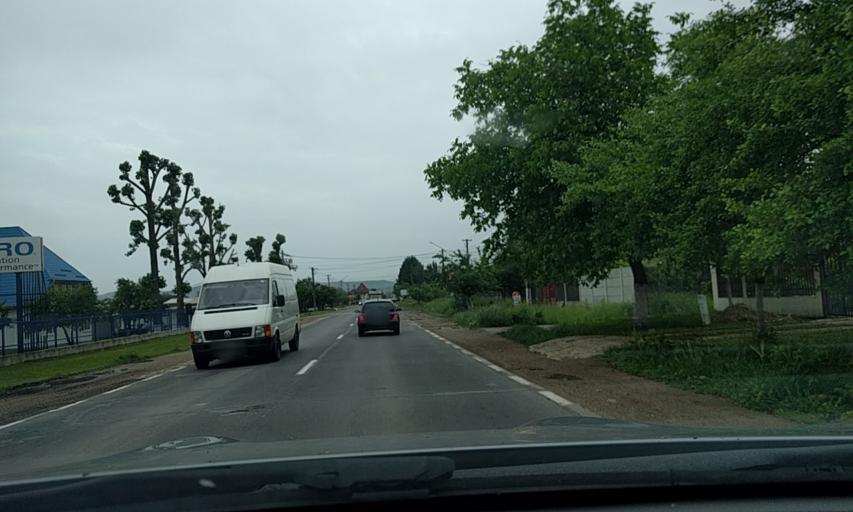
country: RO
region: Dambovita
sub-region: Comuna Aninoasa
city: Sateni
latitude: 44.9858
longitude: 25.4157
